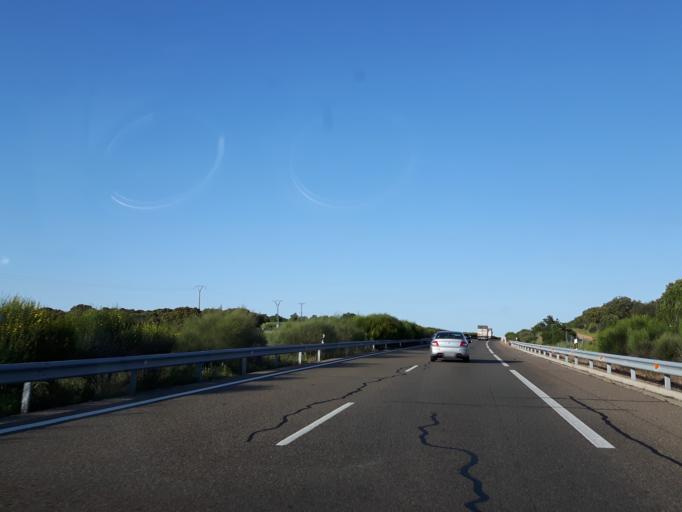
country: ES
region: Castille and Leon
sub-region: Provincia de Salamanca
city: Aldehuela de la Boveda
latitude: 40.8326
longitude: -6.0971
